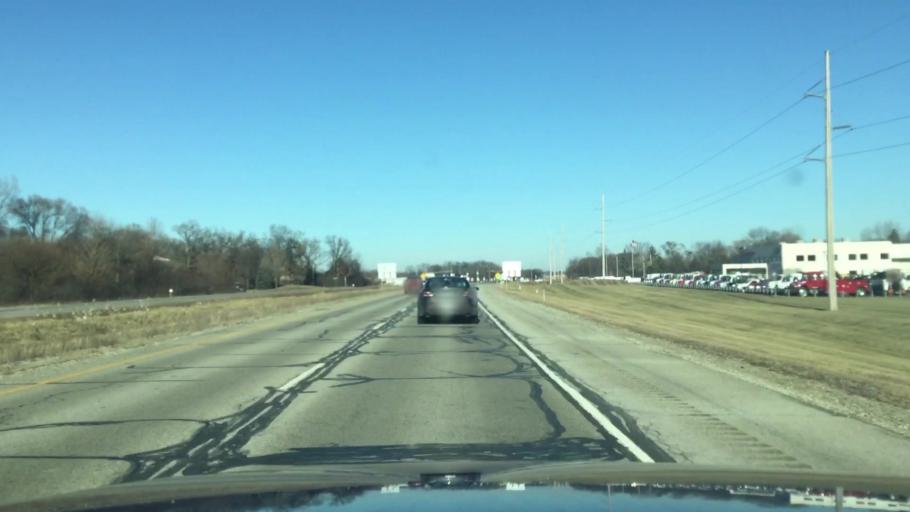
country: US
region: Wisconsin
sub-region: Racine County
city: Waterford
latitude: 42.7491
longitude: -88.2111
